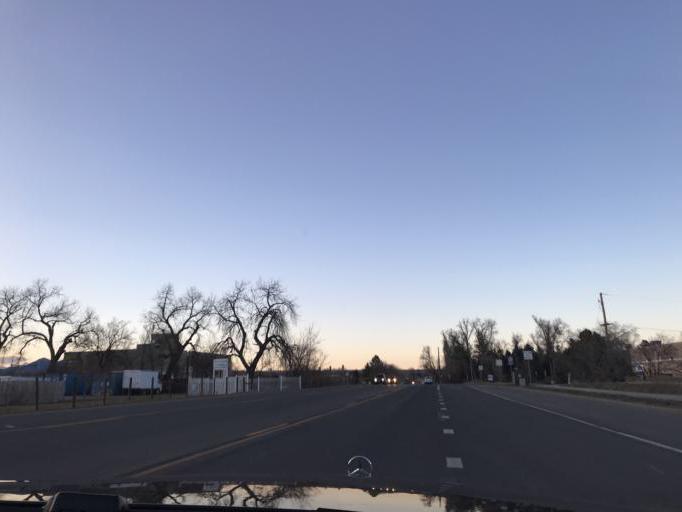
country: US
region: Colorado
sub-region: Jefferson County
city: Applewood
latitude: 39.8153
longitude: -105.1651
